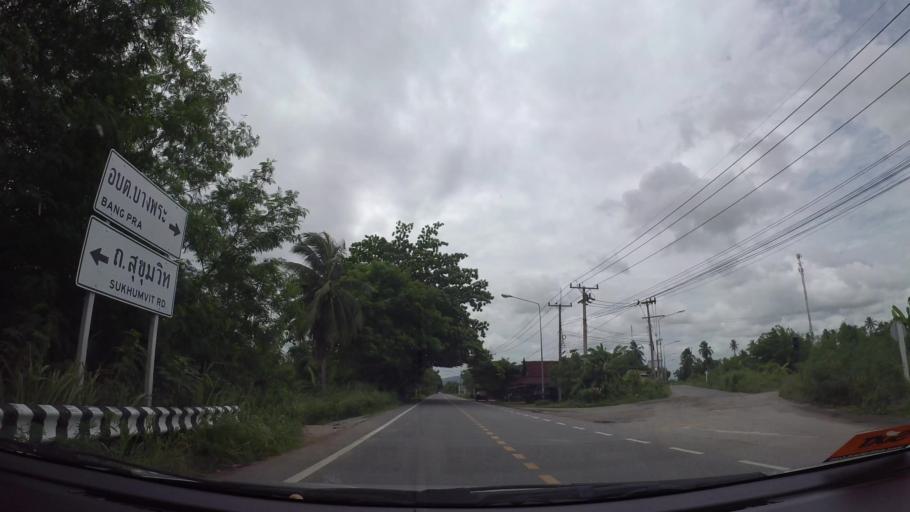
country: TH
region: Chon Buri
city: Si Racha
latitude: 13.1859
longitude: 100.9861
